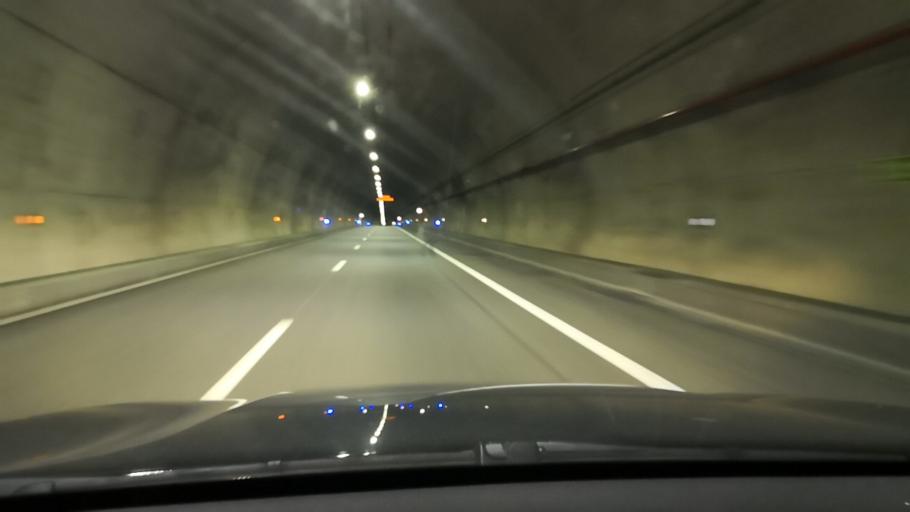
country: PT
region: Vila Real
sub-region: Santa Marta de Penaguiao
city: Santa Marta de Penaguiao
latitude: 41.2776
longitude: -7.8772
